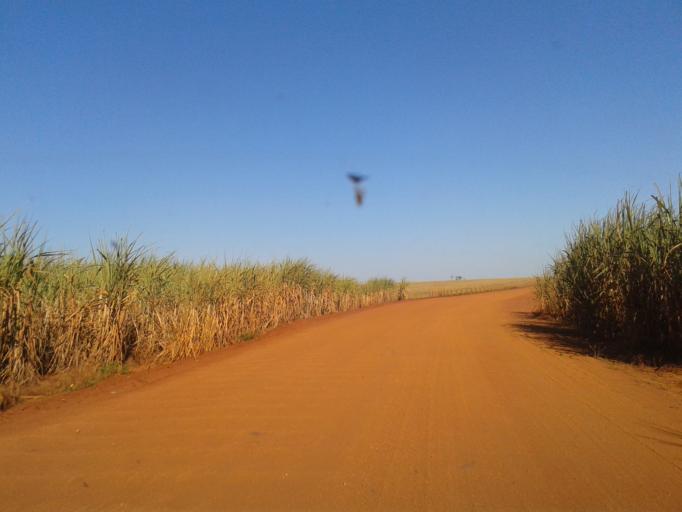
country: BR
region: Minas Gerais
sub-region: Santa Vitoria
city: Santa Vitoria
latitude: -18.8348
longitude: -50.0613
